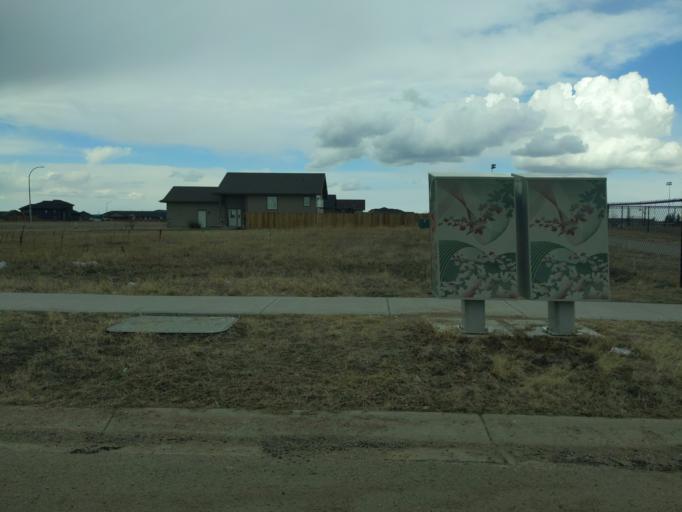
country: CA
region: Saskatchewan
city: Lloydminster
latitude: 53.2691
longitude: -110.0460
